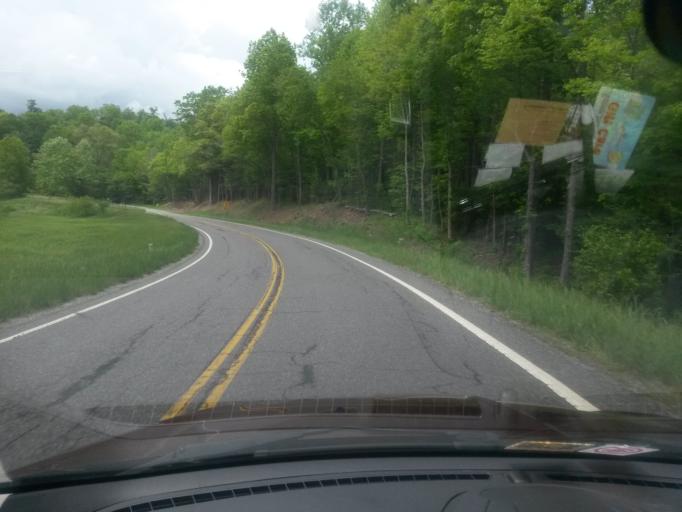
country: US
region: Virginia
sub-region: Floyd County
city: Floyd
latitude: 36.8890
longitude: -80.3221
